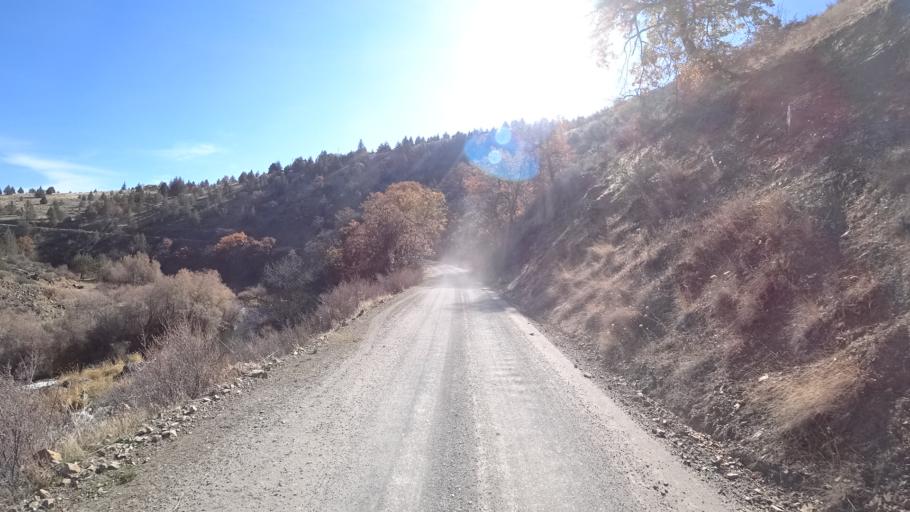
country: US
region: California
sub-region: Siskiyou County
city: Yreka
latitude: 41.7829
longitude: -122.6040
